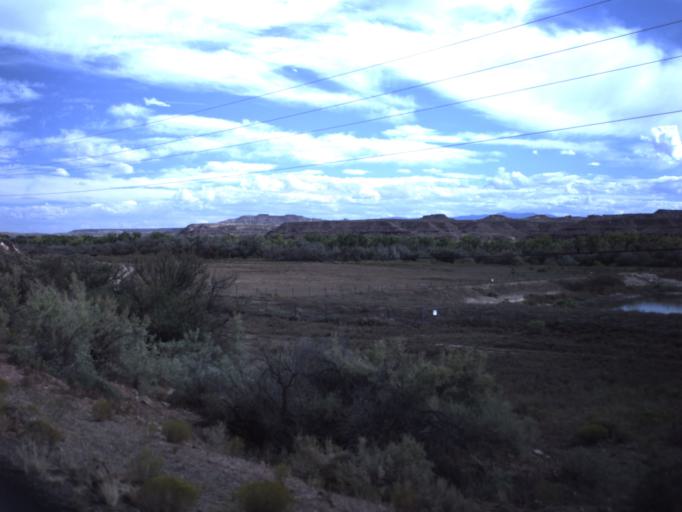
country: US
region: Colorado
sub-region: Montezuma County
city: Towaoc
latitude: 37.2176
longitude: -109.1897
